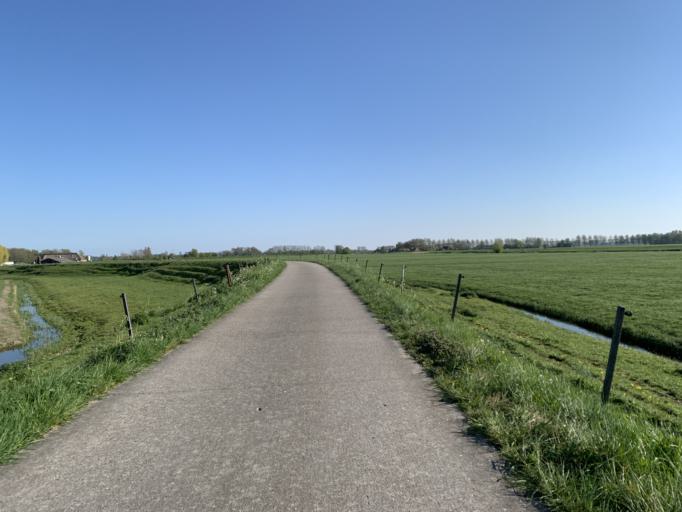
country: NL
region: Groningen
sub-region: Gemeente Zuidhorn
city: Aduard
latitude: 53.2792
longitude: 6.5054
